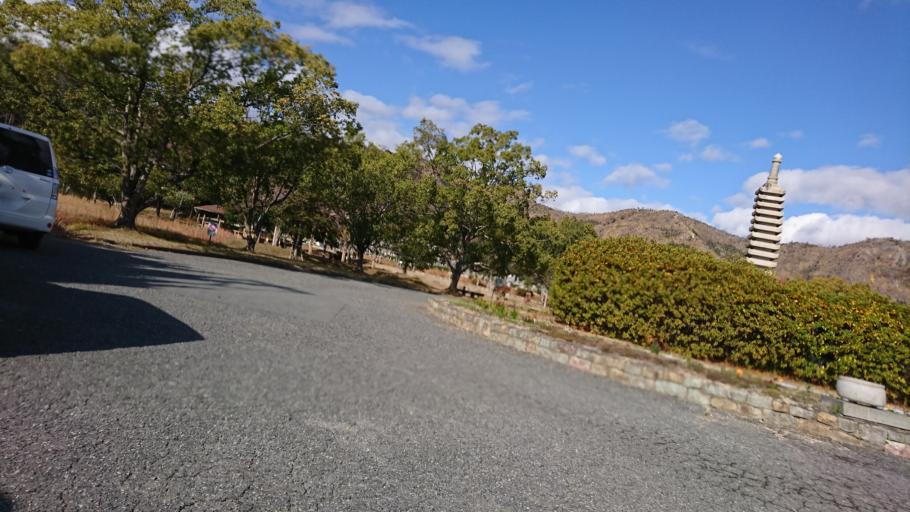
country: JP
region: Hyogo
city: Kakogawacho-honmachi
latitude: 34.8048
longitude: 134.7827
